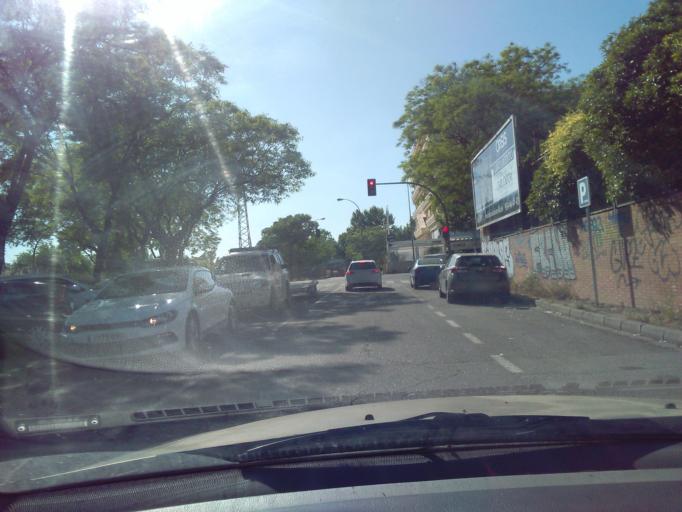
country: ES
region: Andalusia
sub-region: Provincia de Sevilla
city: Sevilla
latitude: 37.4085
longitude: -5.9334
